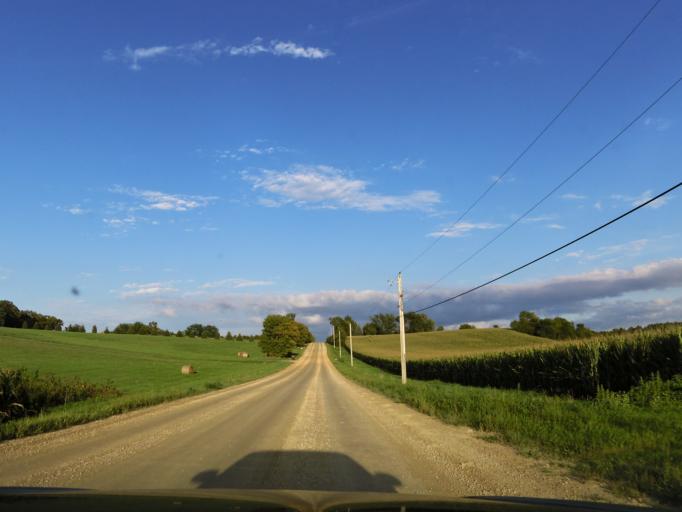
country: US
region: Minnesota
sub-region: Washington County
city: Cottage Grove
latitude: 44.8765
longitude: -92.8769
